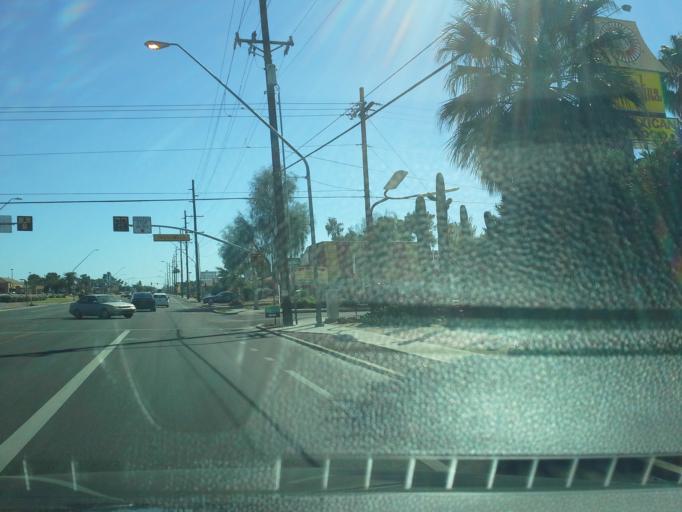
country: US
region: Arizona
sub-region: Pima County
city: Tucson
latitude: 32.2615
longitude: -110.9439
